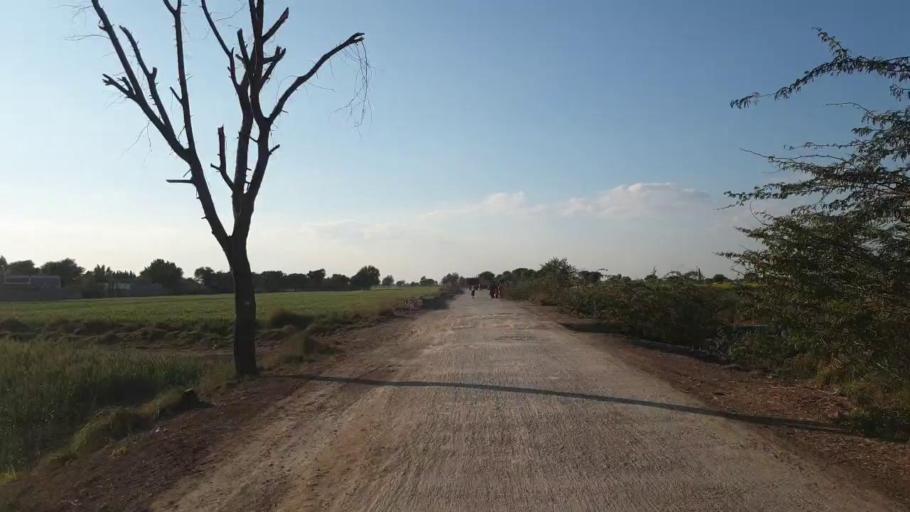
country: PK
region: Sindh
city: Shahpur Chakar
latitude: 26.1360
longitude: 68.5604
